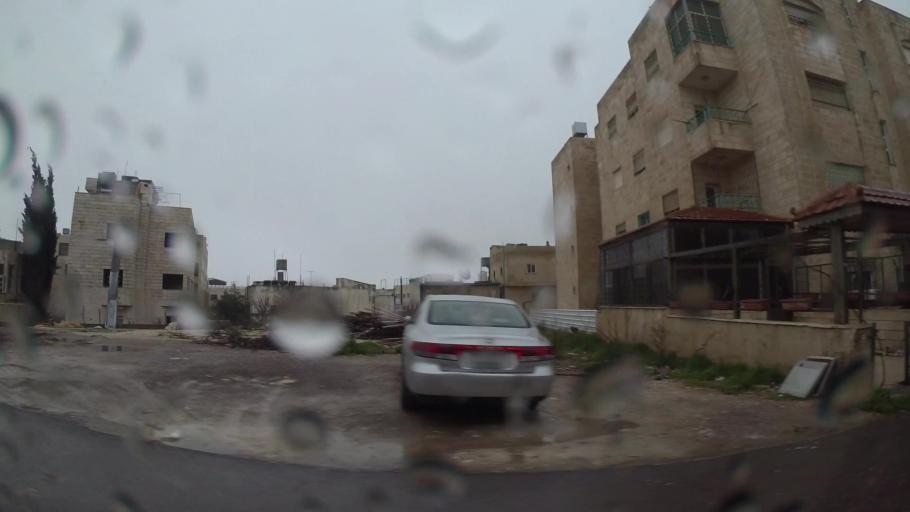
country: JO
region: Amman
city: Al Jubayhah
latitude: 32.0285
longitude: 35.8505
